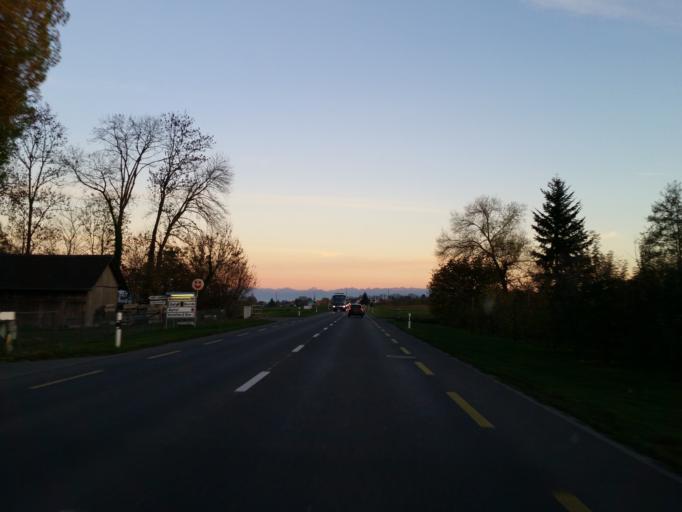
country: CH
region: Thurgau
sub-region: Kreuzlingen District
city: Guttingen
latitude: 47.6001
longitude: 9.2988
